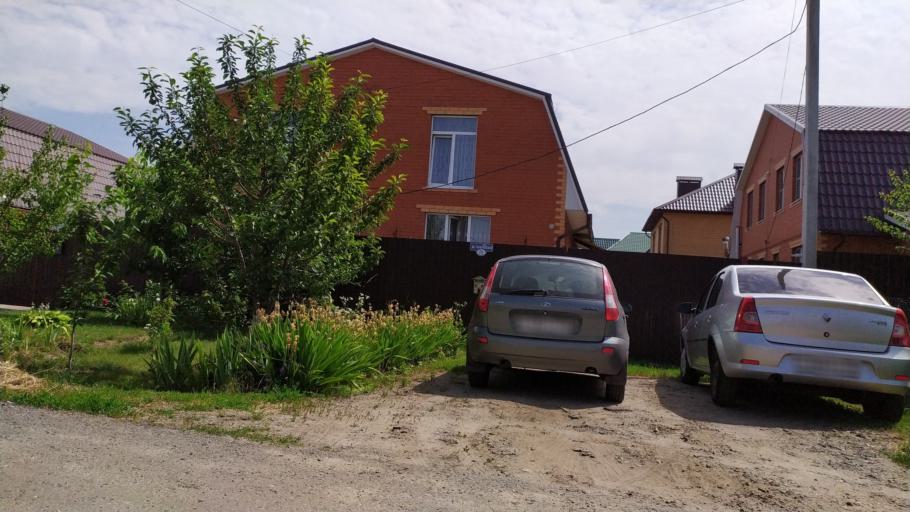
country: RU
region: Kursk
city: Kursk
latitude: 51.6426
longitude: 36.1360
